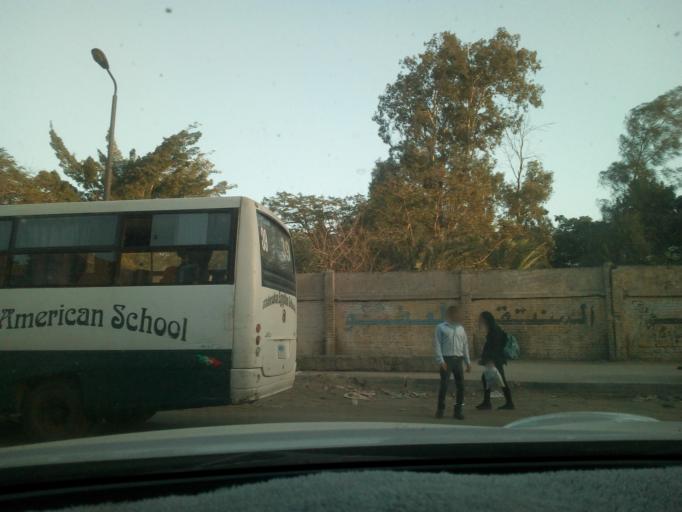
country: EG
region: Muhafazat al Qalyubiyah
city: Al Khankah
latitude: 30.1239
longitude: 31.3465
